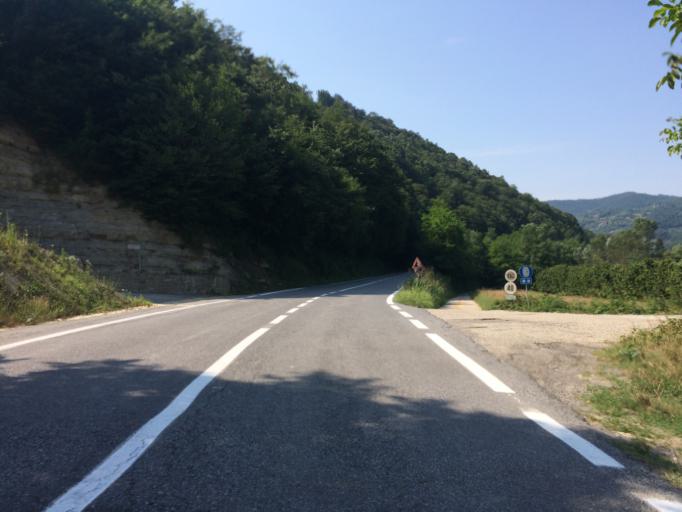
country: IT
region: Piedmont
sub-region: Provincia di Cuneo
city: Torre Bormida
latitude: 44.5637
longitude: 8.1720
